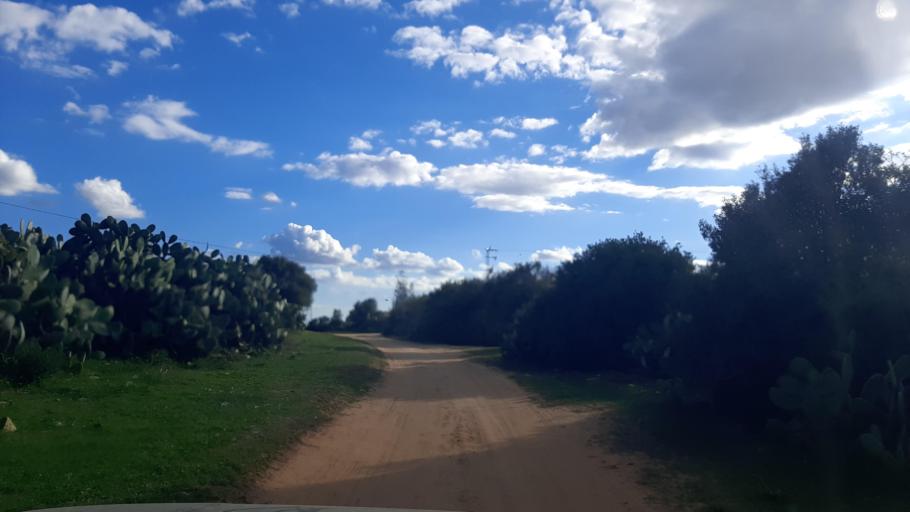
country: TN
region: Nabul
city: Bu `Urqub
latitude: 36.4431
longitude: 10.5066
